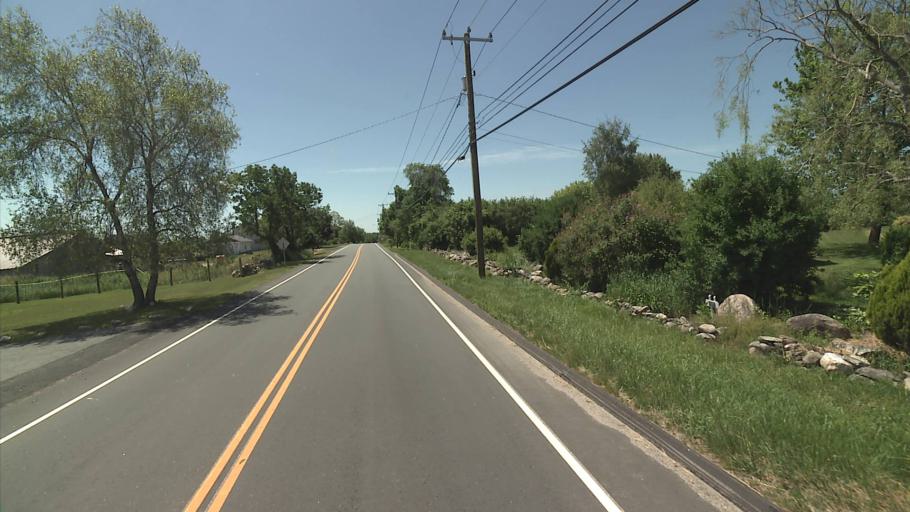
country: US
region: Connecticut
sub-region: Windham County
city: Plainfield
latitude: 41.6454
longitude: -71.8473
